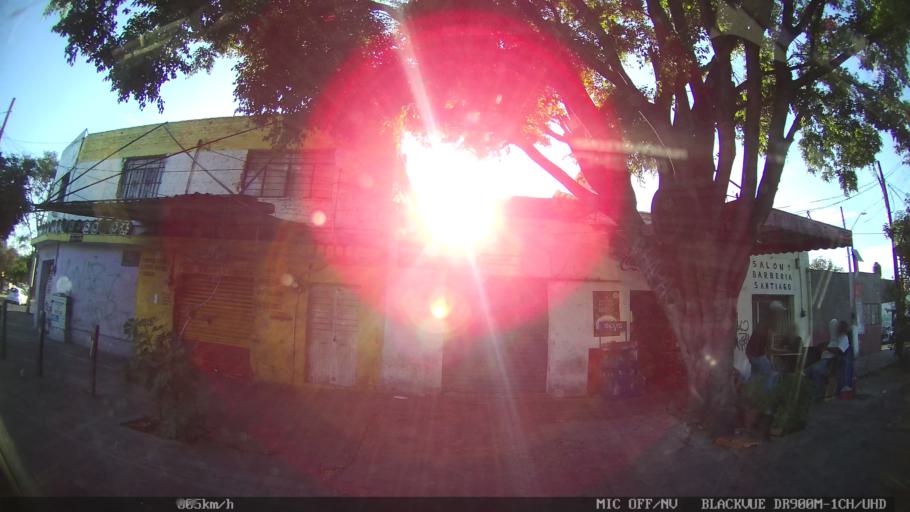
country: MX
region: Jalisco
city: Tlaquepaque
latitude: 20.6957
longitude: -103.3025
